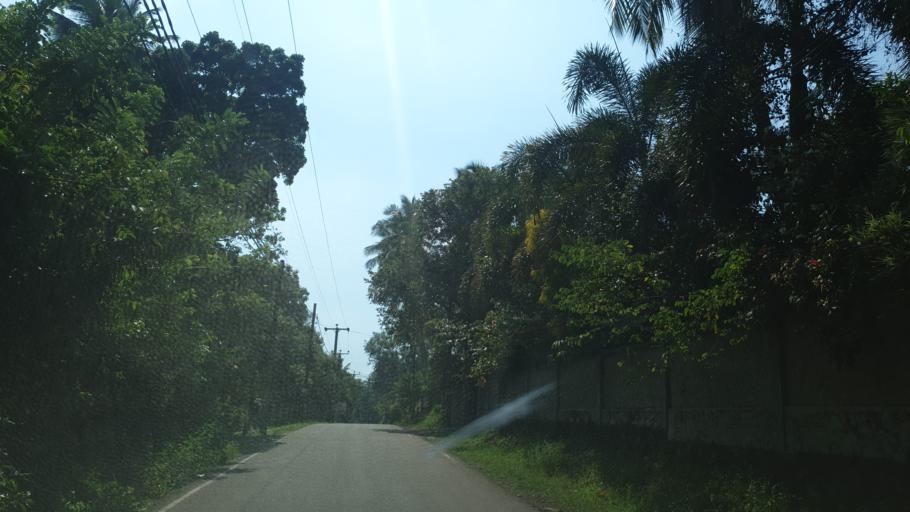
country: LK
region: Western
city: Moratuwa
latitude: 6.7637
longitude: 79.9298
